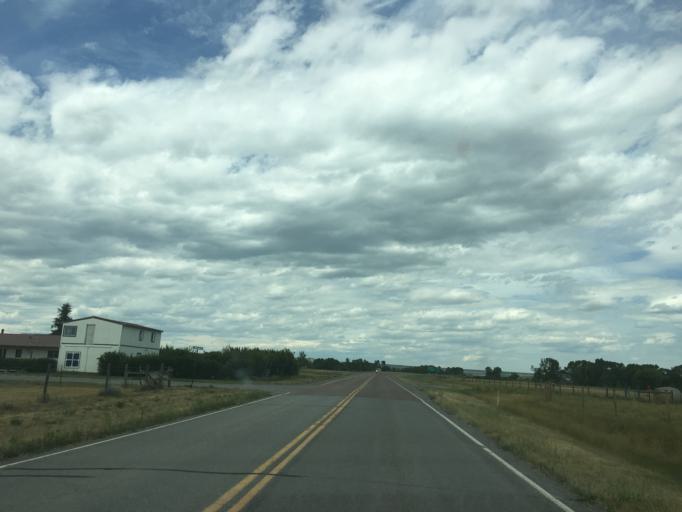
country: US
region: Montana
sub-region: Teton County
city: Choteau
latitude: 47.9802
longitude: -112.3136
